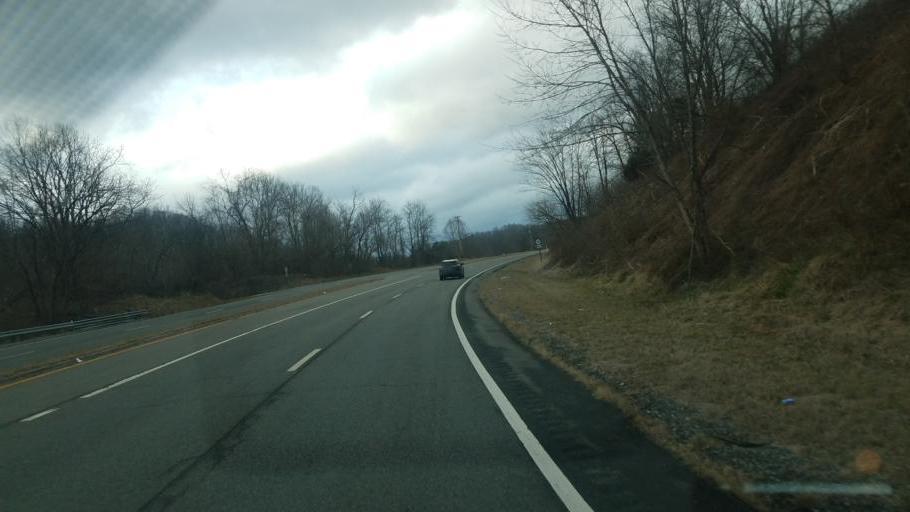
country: US
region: Virginia
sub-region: Giles County
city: Pearisburg
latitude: 37.2585
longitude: -80.7120
